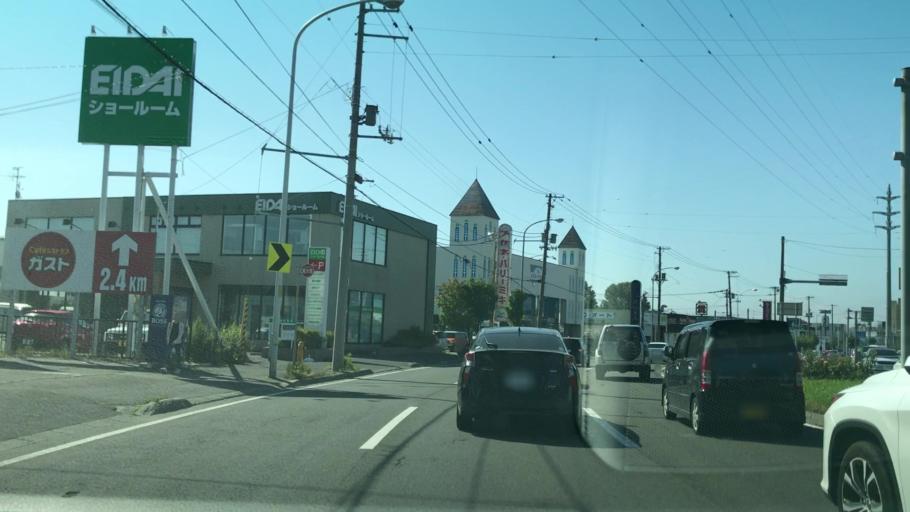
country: JP
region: Hokkaido
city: Sapporo
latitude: 43.0711
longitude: 141.4087
